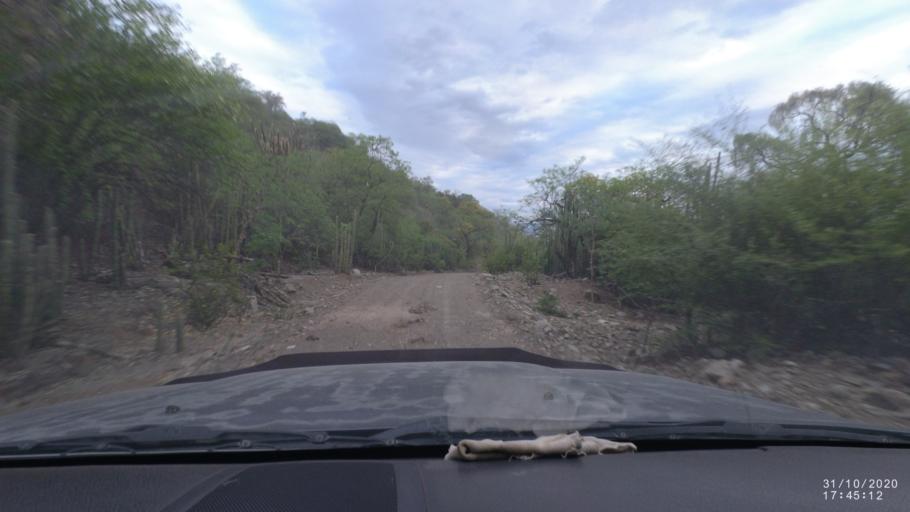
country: BO
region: Chuquisaca
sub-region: Provincia Zudanez
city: Mojocoya
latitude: -18.6140
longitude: -64.5436
